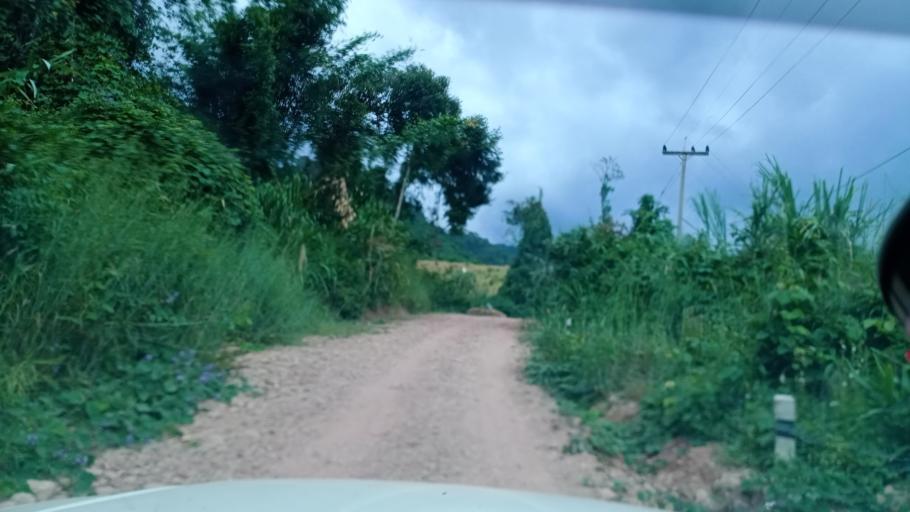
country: TH
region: Changwat Bueng Kan
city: Pak Khat
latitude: 18.7257
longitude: 103.2629
